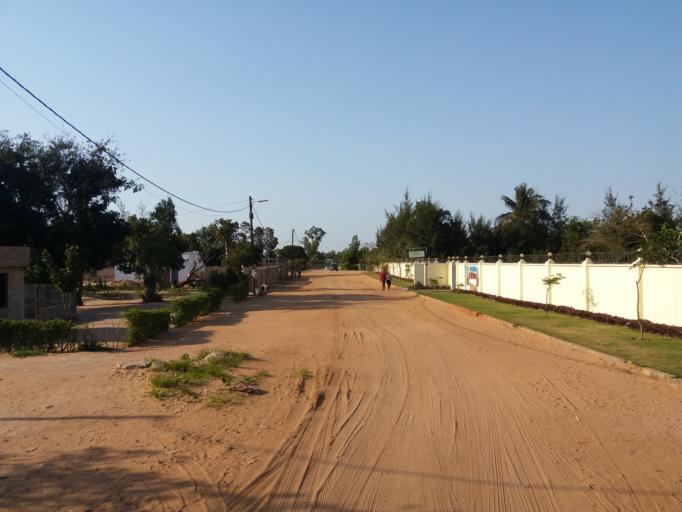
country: MZ
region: Maputo City
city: Maputo
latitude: -25.7646
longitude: 32.6085
